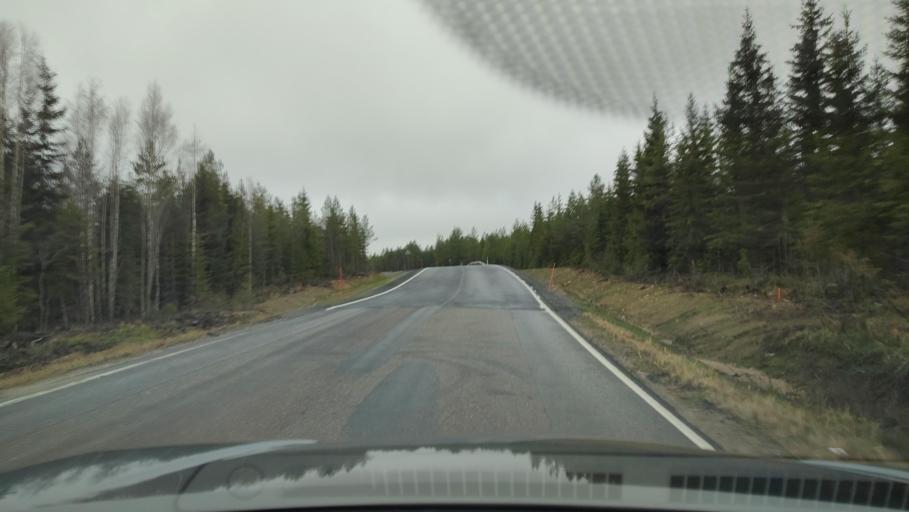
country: FI
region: Southern Ostrobothnia
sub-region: Suupohja
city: Kauhajoki
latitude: 62.2925
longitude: 22.0525
